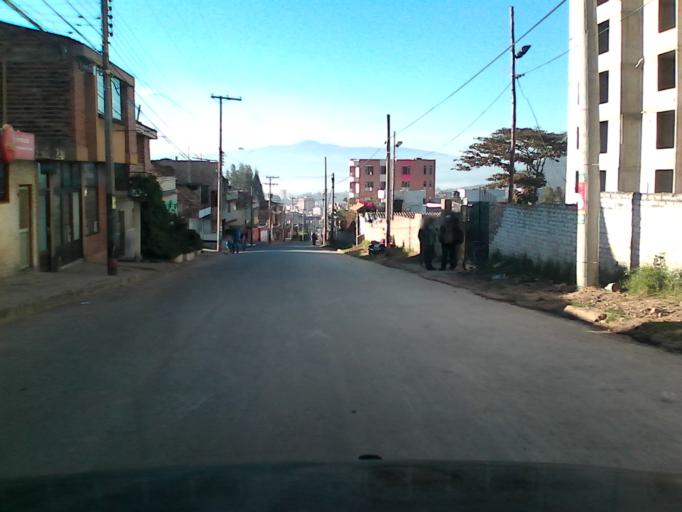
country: CO
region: Boyaca
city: Duitama
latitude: 5.8424
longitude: -73.0369
